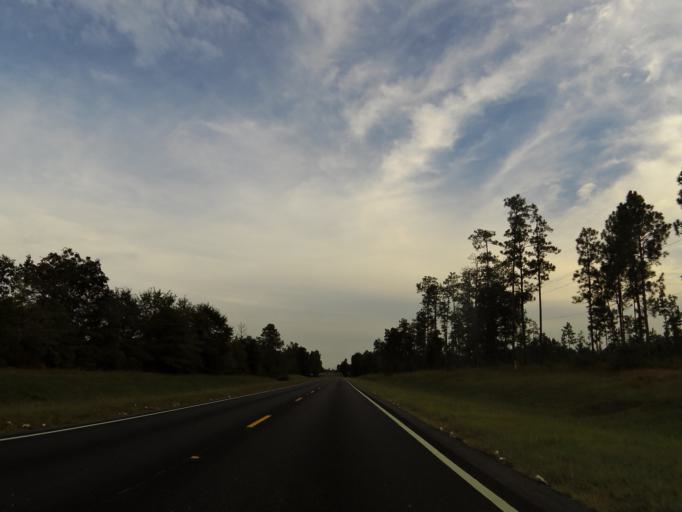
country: US
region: Alabama
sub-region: Monroe County
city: Frisco City
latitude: 31.2419
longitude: -87.4868
